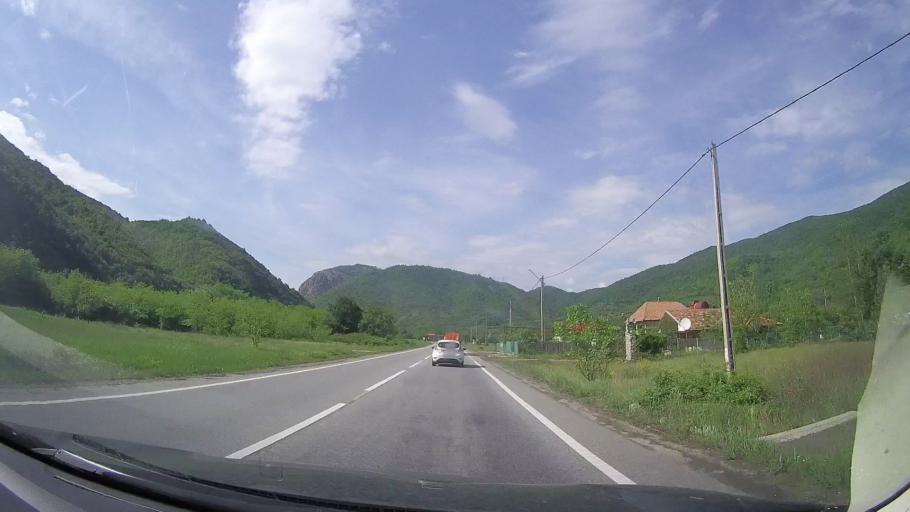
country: RO
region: Caras-Severin
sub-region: Comuna Mehadia
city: Mehadia
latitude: 44.8807
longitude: 22.3838
